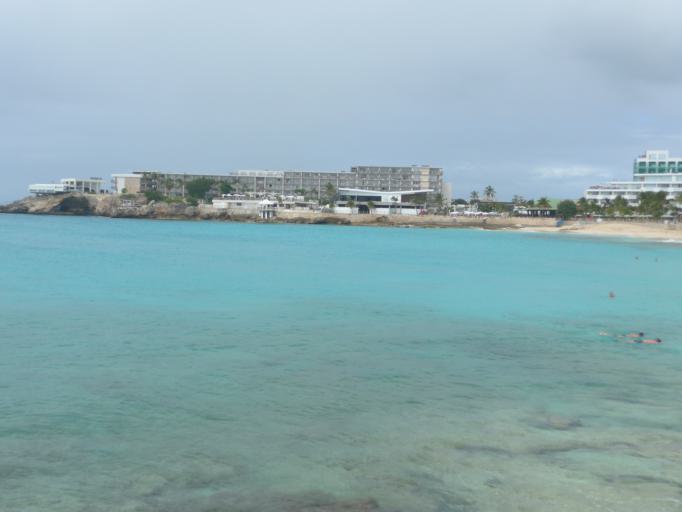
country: MF
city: Marigot
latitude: 18.0384
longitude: -63.1204
